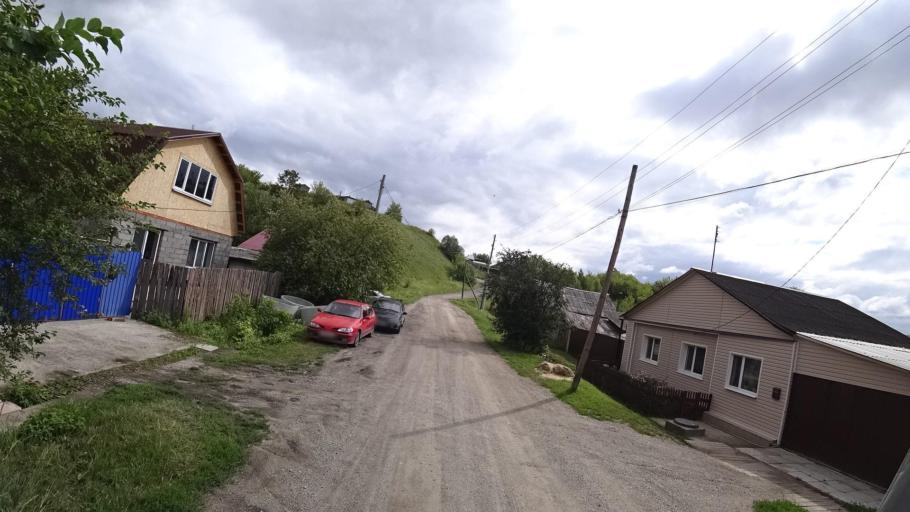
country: RU
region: Sverdlovsk
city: Kamyshlov
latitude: 56.8573
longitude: 62.7186
